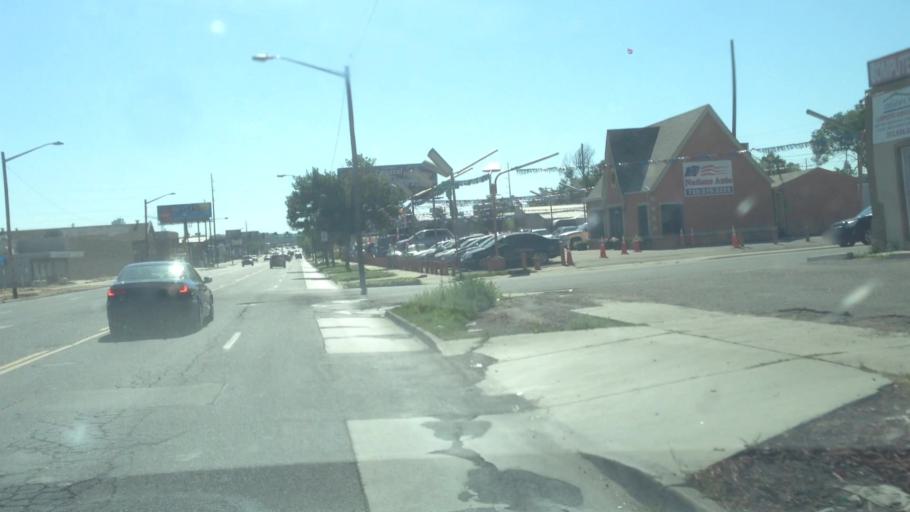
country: US
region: Colorado
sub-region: Denver County
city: Denver
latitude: 39.7111
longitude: -105.0091
